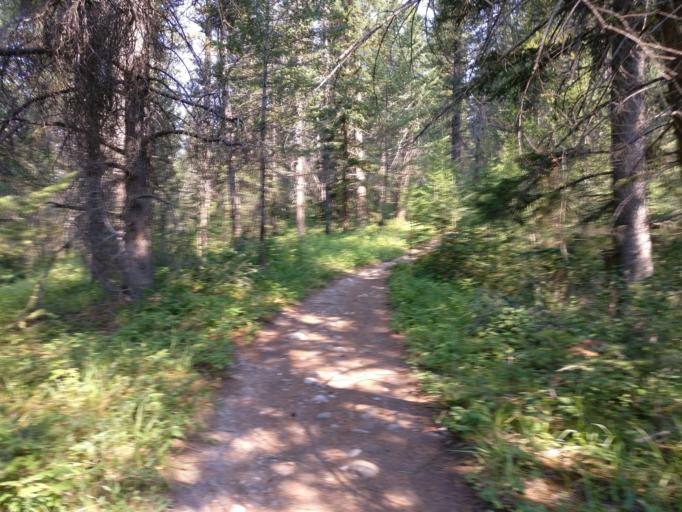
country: CA
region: Alberta
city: Canmore
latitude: 51.0829
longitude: -115.3207
